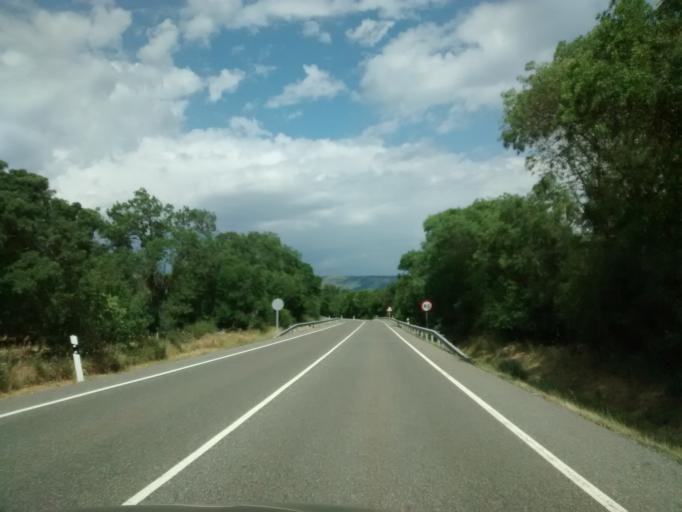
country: ES
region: Castille and Leon
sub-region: Provincia de Segovia
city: Matabuena
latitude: 41.0931
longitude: -3.7708
